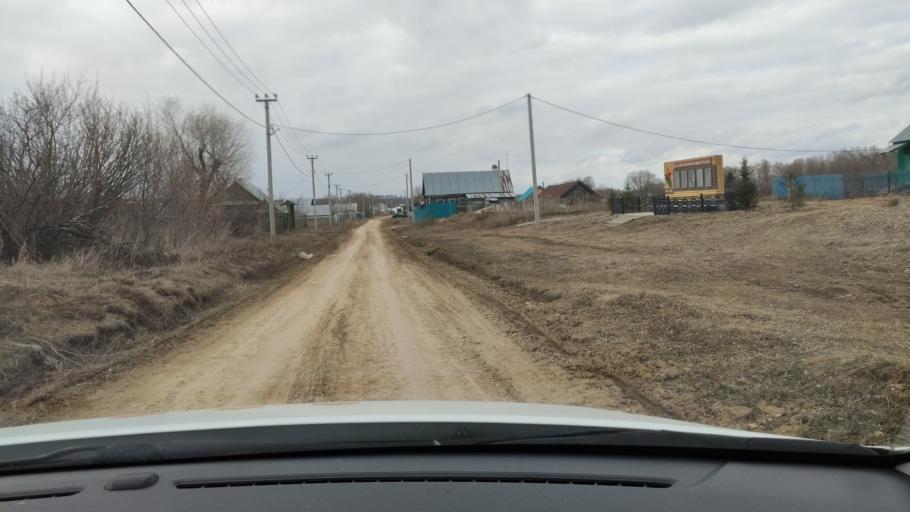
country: RU
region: Tatarstan
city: Vysokaya Gora
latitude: 56.2128
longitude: 49.3131
